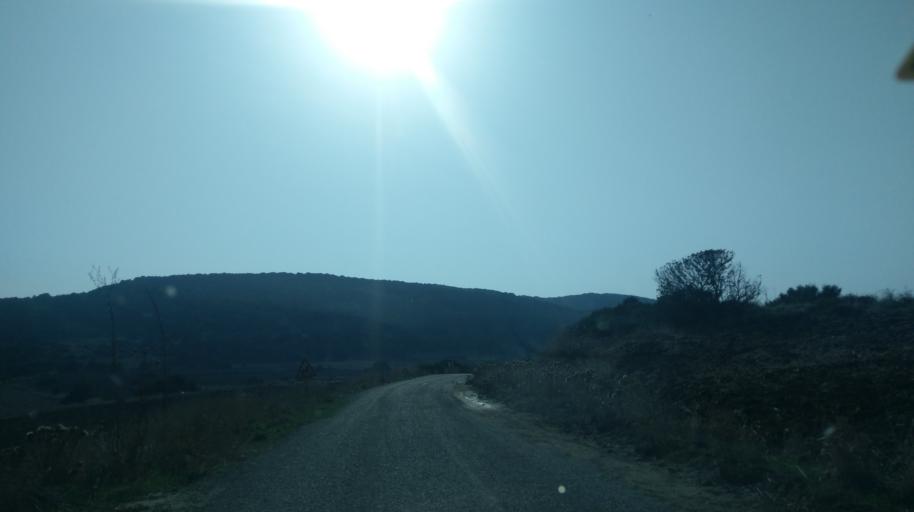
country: CY
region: Ammochostos
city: Rizokarpaso
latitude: 35.5549
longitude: 34.3684
